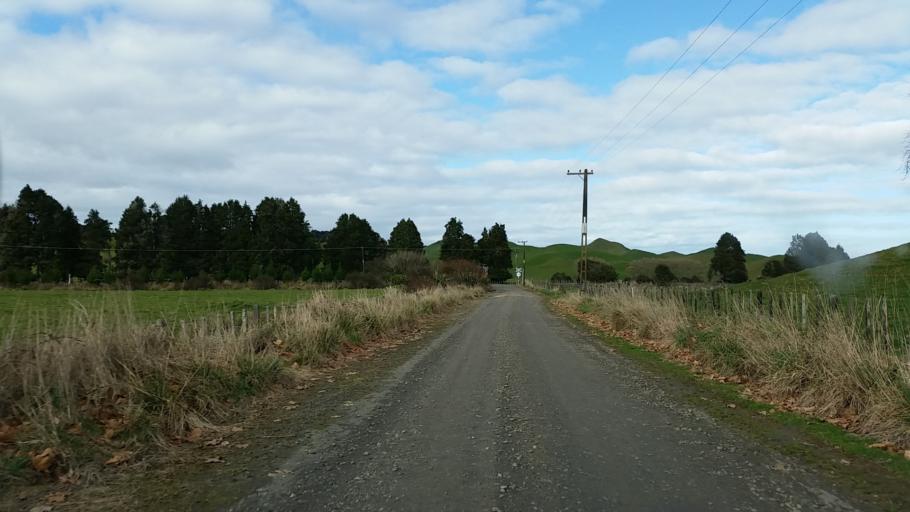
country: NZ
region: Taranaki
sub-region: South Taranaki District
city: Eltham
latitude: -39.2331
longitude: 174.5200
